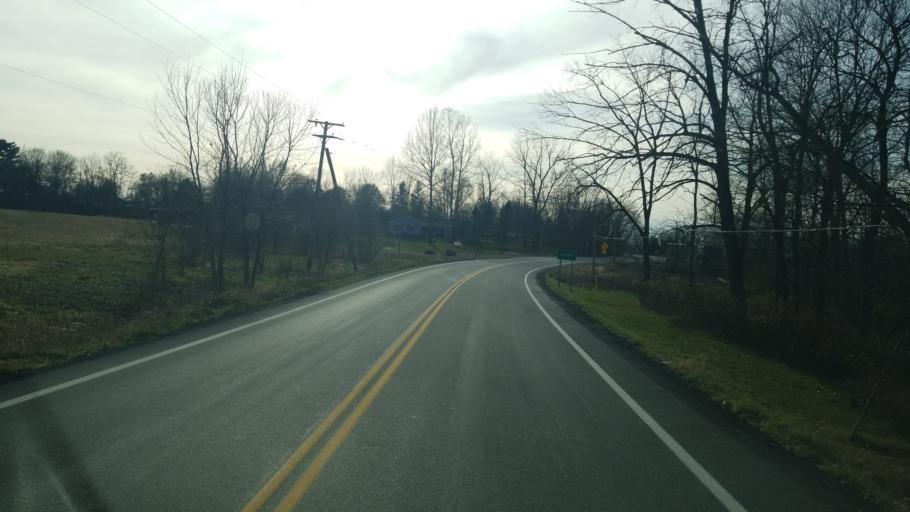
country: US
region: Ohio
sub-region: Ashland County
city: Ashland
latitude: 40.9266
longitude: -82.2788
